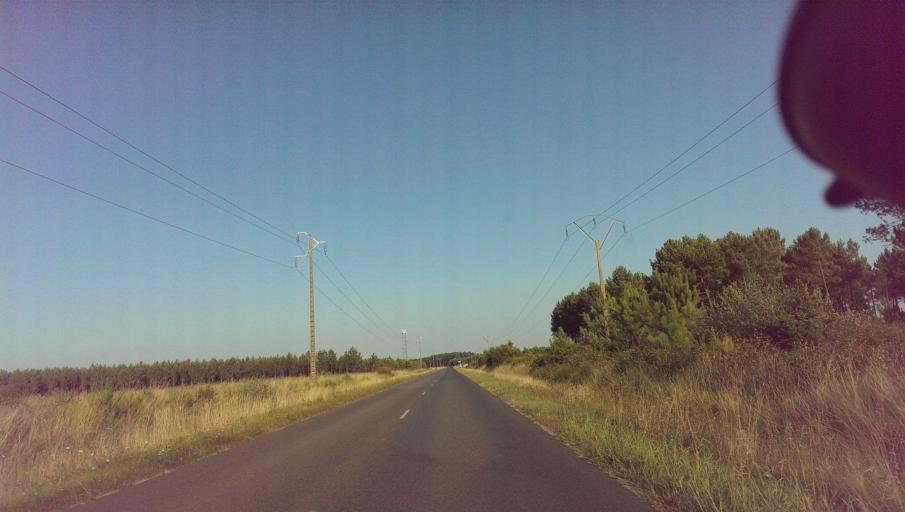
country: FR
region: Aquitaine
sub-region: Departement des Landes
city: Mimizan
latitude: 44.1814
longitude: -1.1764
